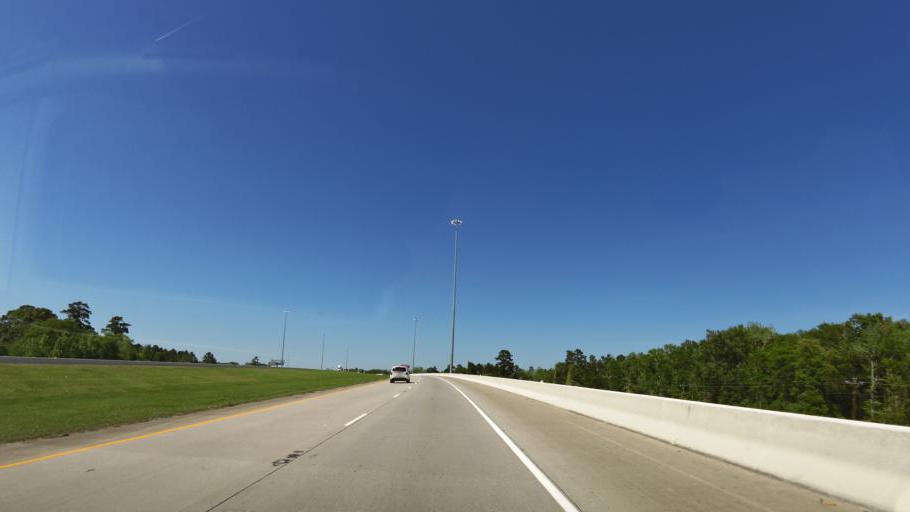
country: US
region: Texas
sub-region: San Jacinto County
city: Shepherd
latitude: 30.4973
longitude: -94.9893
